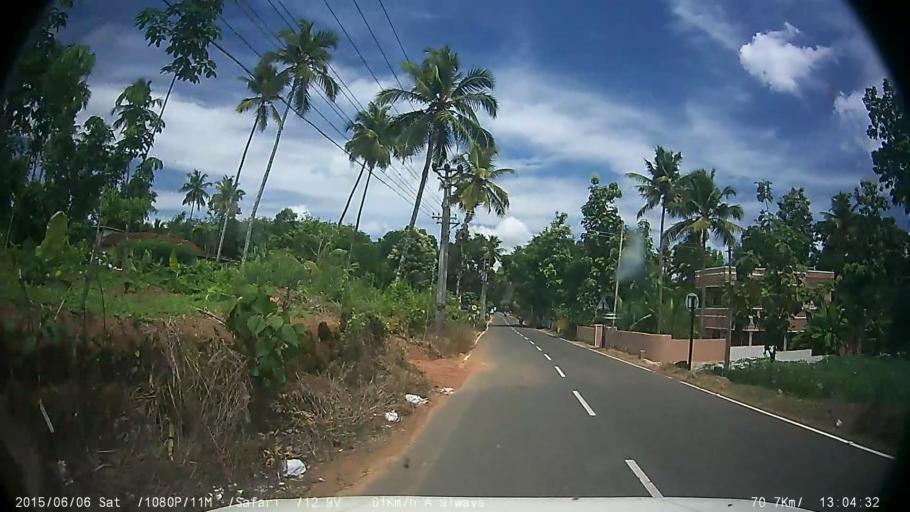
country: IN
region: Kerala
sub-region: Kottayam
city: Changanacheri
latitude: 9.4551
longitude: 76.5768
